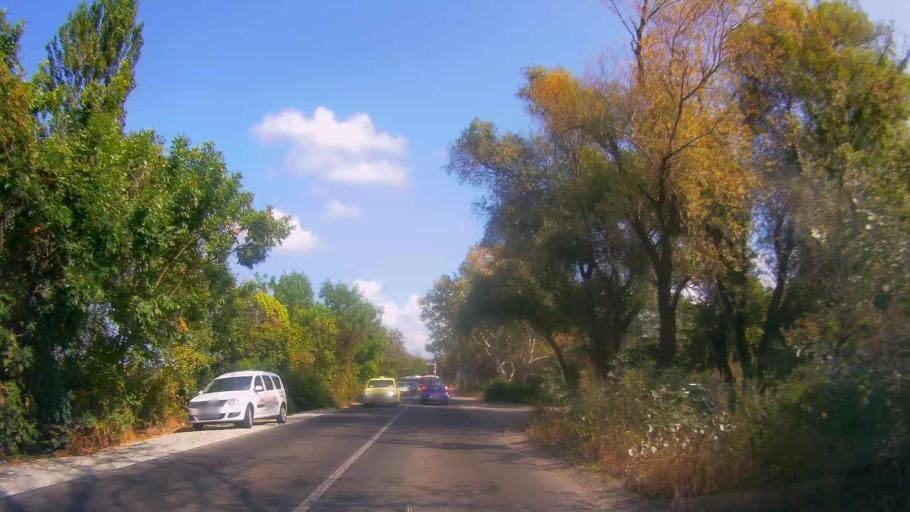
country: BG
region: Burgas
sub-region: Obshtina Burgas
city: Burgas
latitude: 42.4730
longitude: 27.4251
